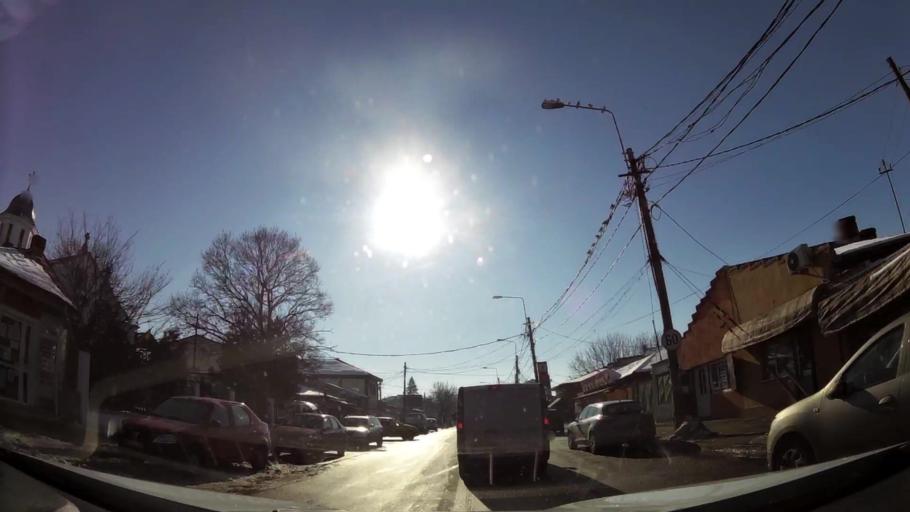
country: RO
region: Ilfov
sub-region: Comuna Magurele
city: Magurele
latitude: 44.3994
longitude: 26.0488
